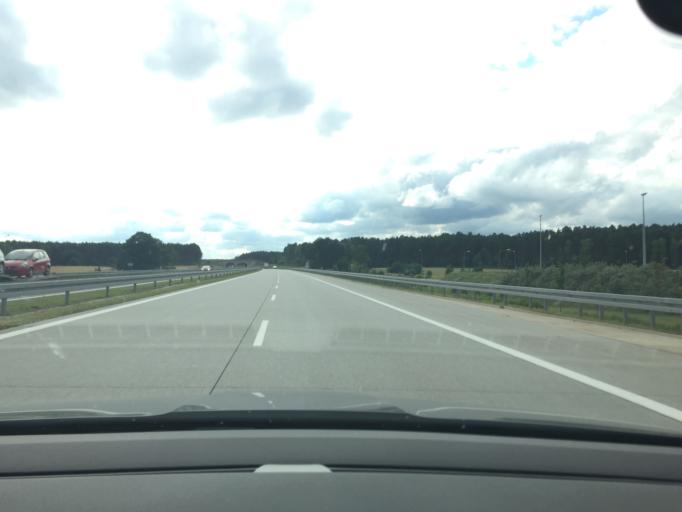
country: PL
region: Lubusz
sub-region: Powiat sulecinski
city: Torzym
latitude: 52.3258
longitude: 15.1636
